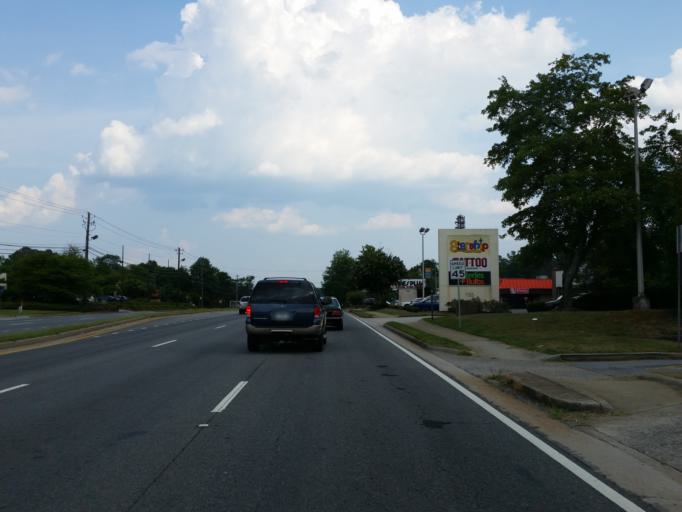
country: US
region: Georgia
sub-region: Fulton County
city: Roswell
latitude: 34.0317
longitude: -84.3398
